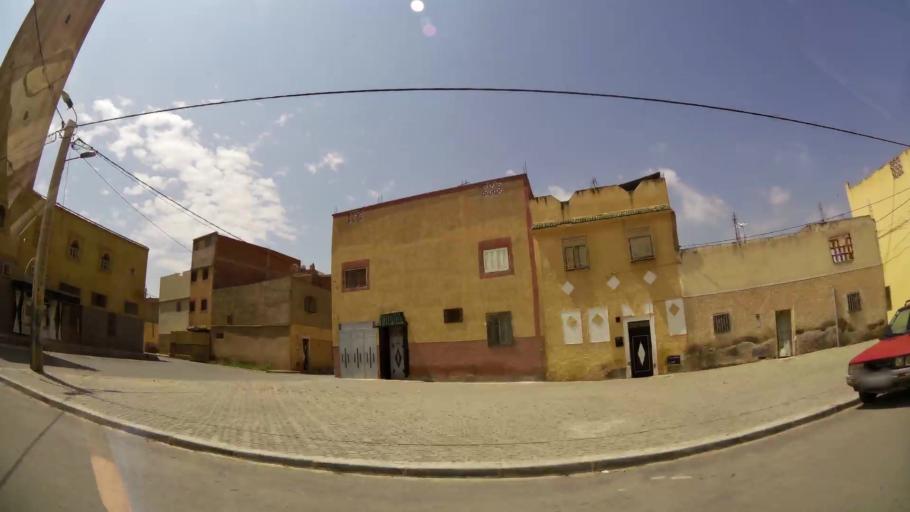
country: MA
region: Oriental
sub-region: Oujda-Angad
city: Oujda
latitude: 34.6855
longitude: -1.8850
